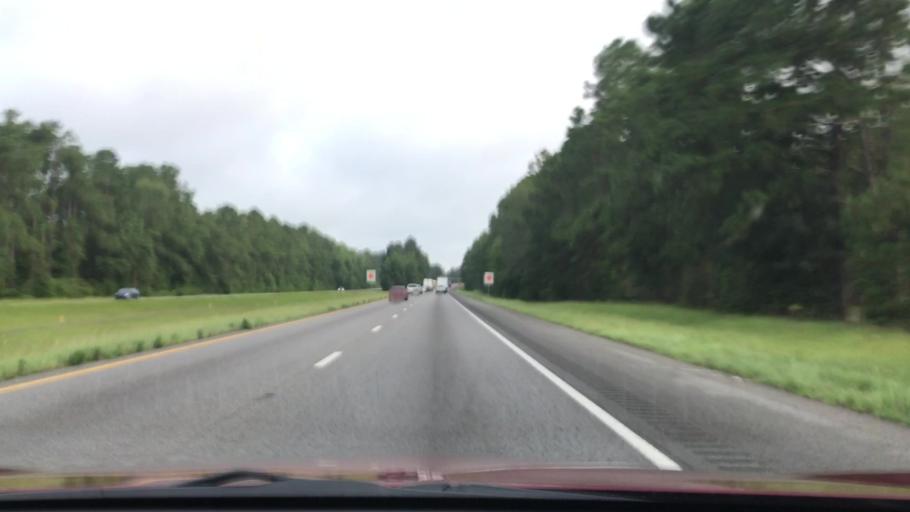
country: US
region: South Carolina
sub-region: Dorchester County
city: Ridgeville
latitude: 33.1827
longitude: -80.3799
